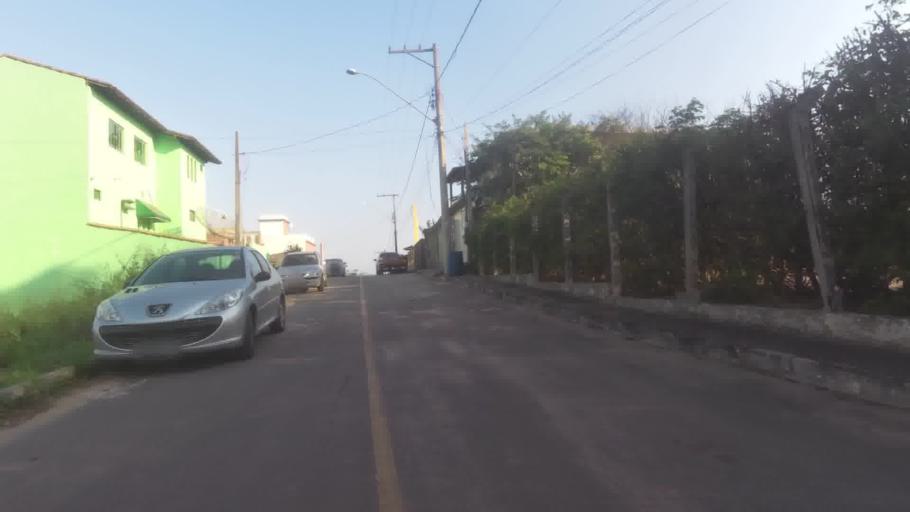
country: BR
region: Espirito Santo
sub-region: Itapemirim
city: Itapemirim
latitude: -21.0191
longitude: -40.8192
